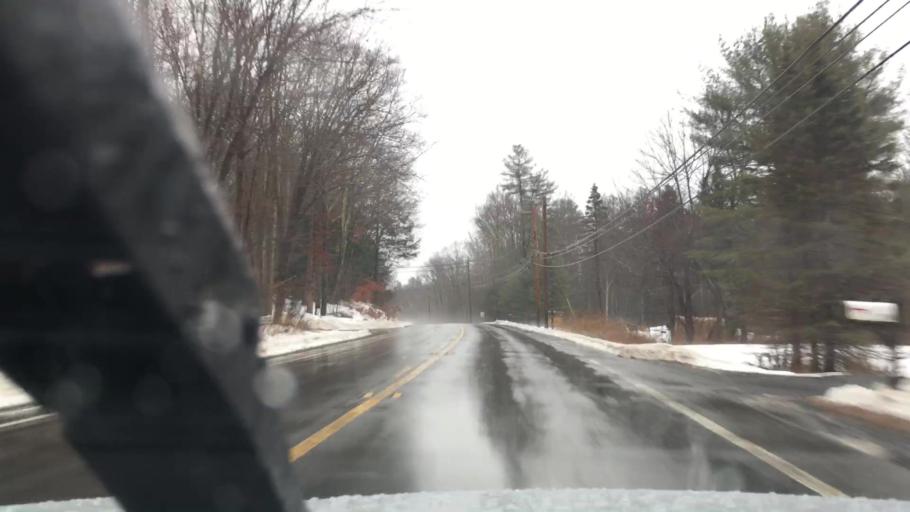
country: US
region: Massachusetts
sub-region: Hampshire County
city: Belchertown
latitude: 42.3033
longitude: -72.4062
